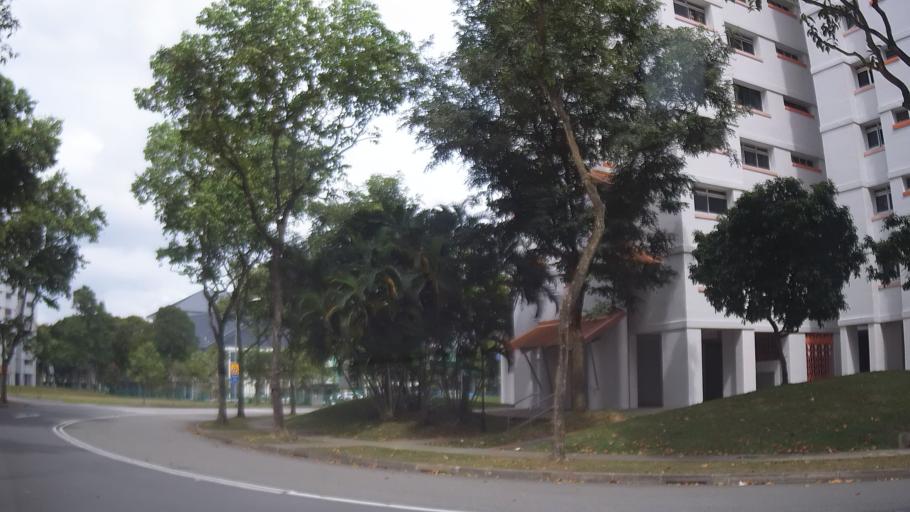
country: MY
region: Johor
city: Johor Bahru
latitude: 1.3894
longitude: 103.7428
